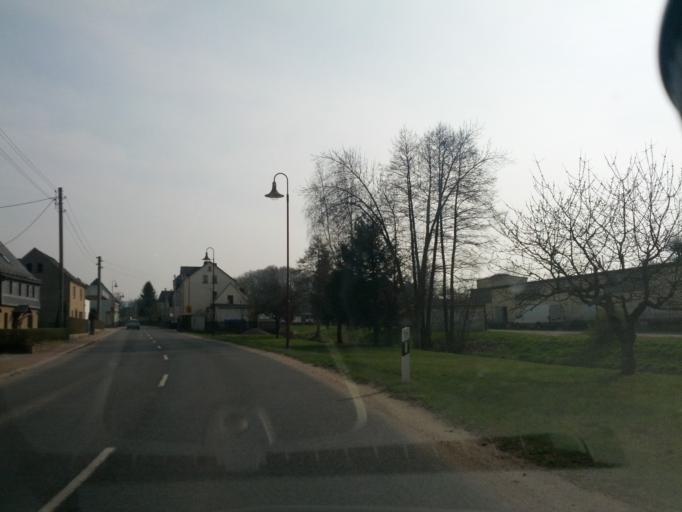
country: DE
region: Saxony
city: Kirchberg
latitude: 50.6006
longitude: 12.5468
